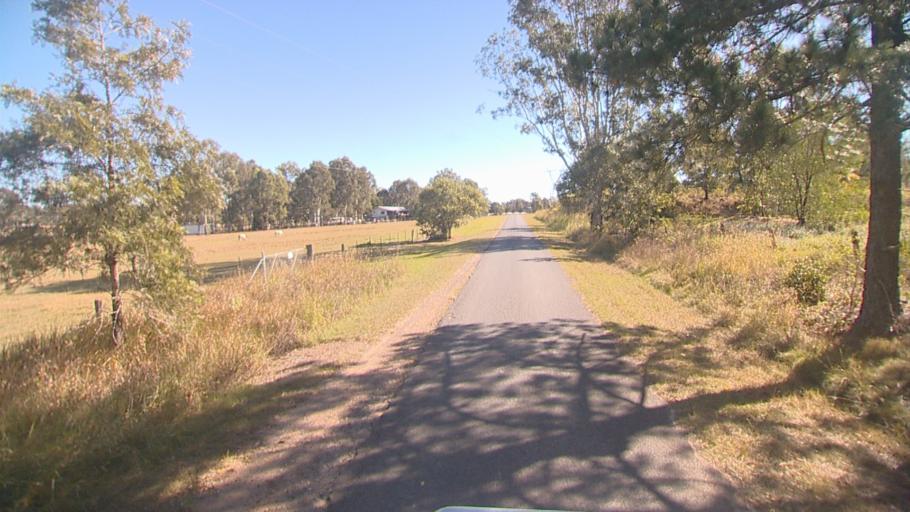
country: AU
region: Queensland
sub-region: Logan
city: North Maclean
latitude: -27.7668
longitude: 153.0257
